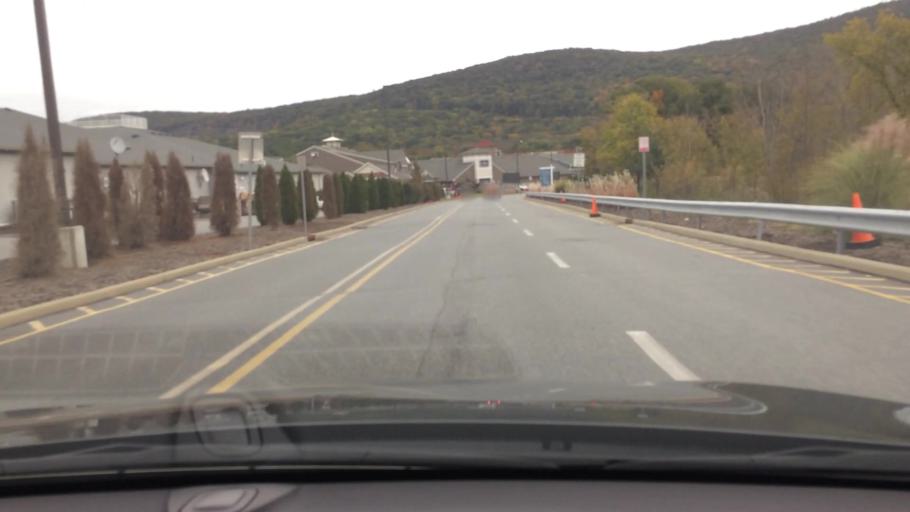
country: US
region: New York
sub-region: Orange County
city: Harriman
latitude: 41.3154
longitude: -74.1300
